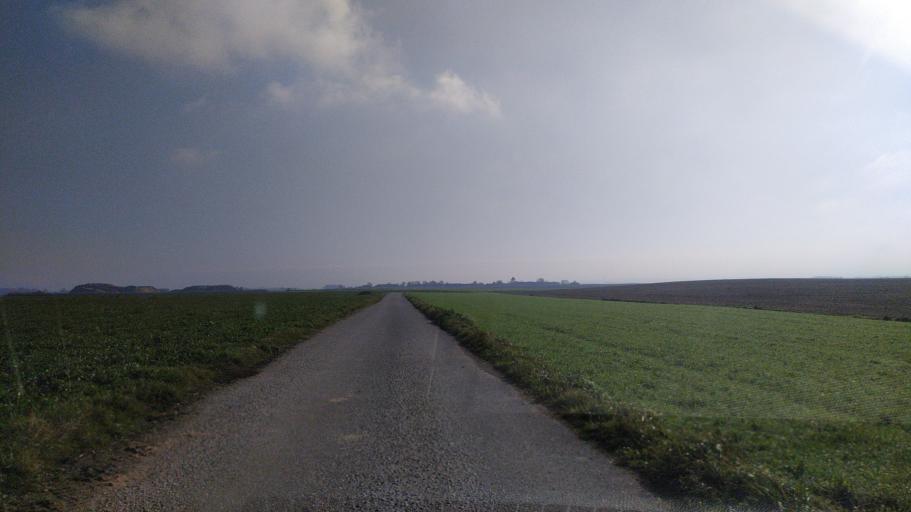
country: AT
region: Upper Austria
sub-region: Politischer Bezirk Perg
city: Perg
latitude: 48.2015
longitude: 14.6405
